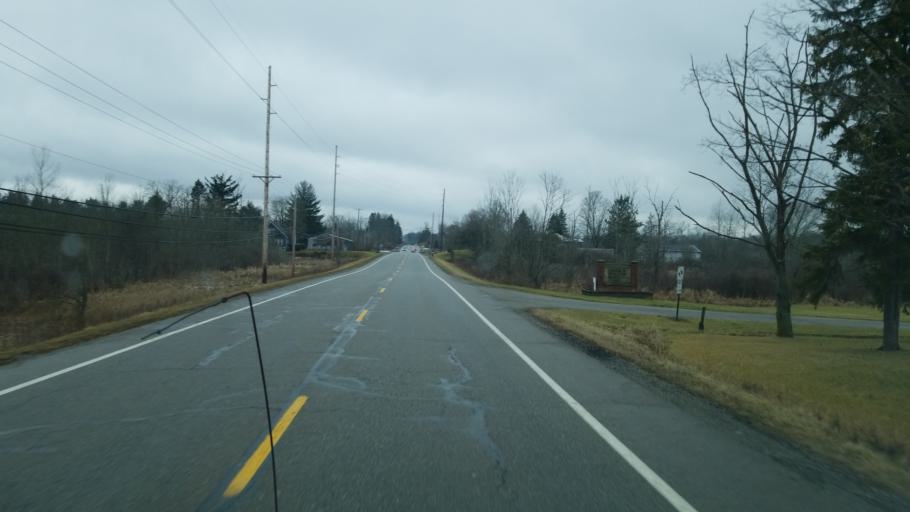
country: US
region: Ohio
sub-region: Portage County
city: Streetsboro
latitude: 41.2396
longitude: -81.3629
